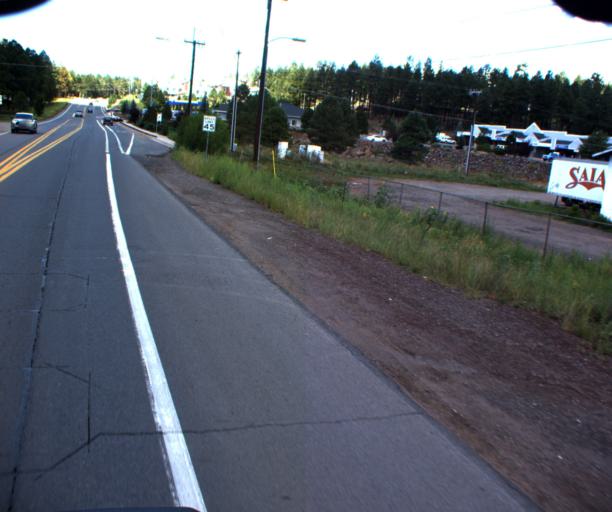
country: US
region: Arizona
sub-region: Coconino County
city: Flagstaff
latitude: 35.1878
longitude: -111.6787
